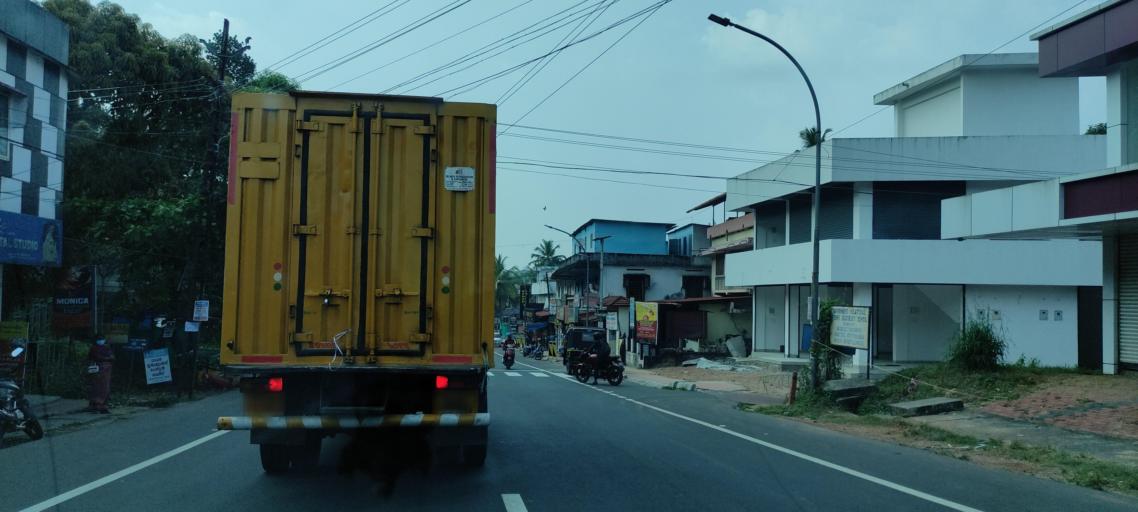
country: IN
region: Kerala
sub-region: Alappuzha
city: Chengannur
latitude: 9.2916
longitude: 76.6480
